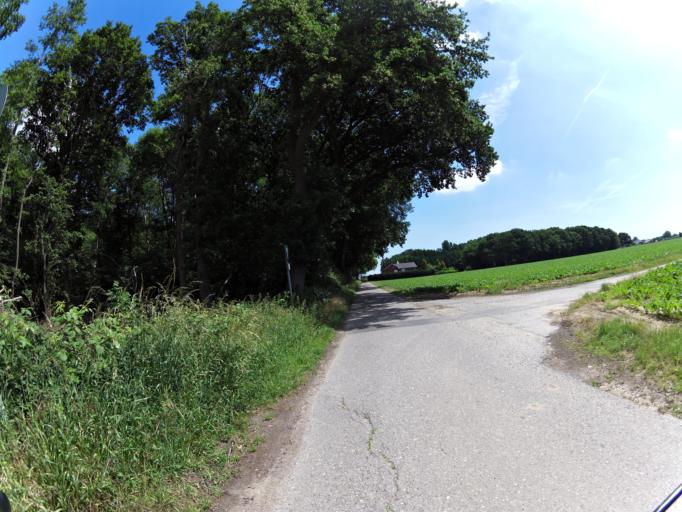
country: DE
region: North Rhine-Westphalia
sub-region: Regierungsbezirk Koln
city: Selfkant
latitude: 51.0264
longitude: 5.9482
